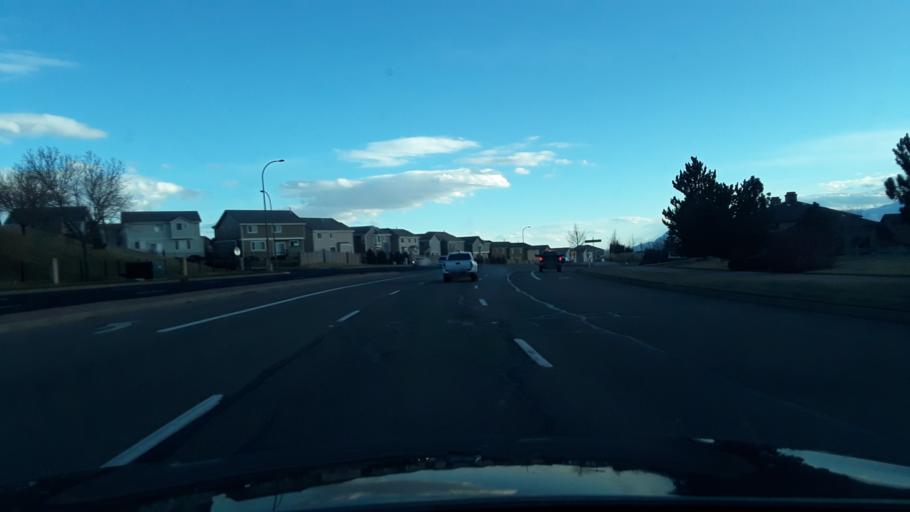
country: US
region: Colorado
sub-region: El Paso County
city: Gleneagle
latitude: 39.0050
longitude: -104.7969
